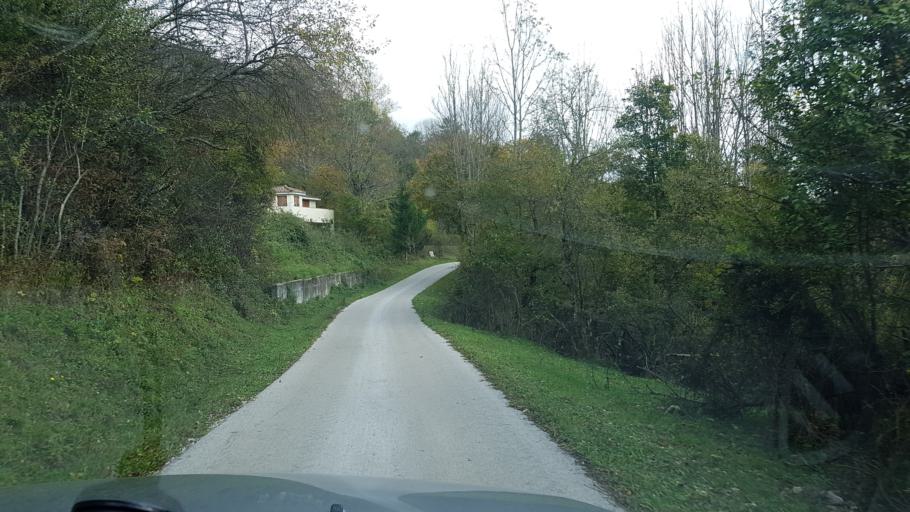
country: HR
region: Istarska
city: Buzet
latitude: 45.4226
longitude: 14.0787
